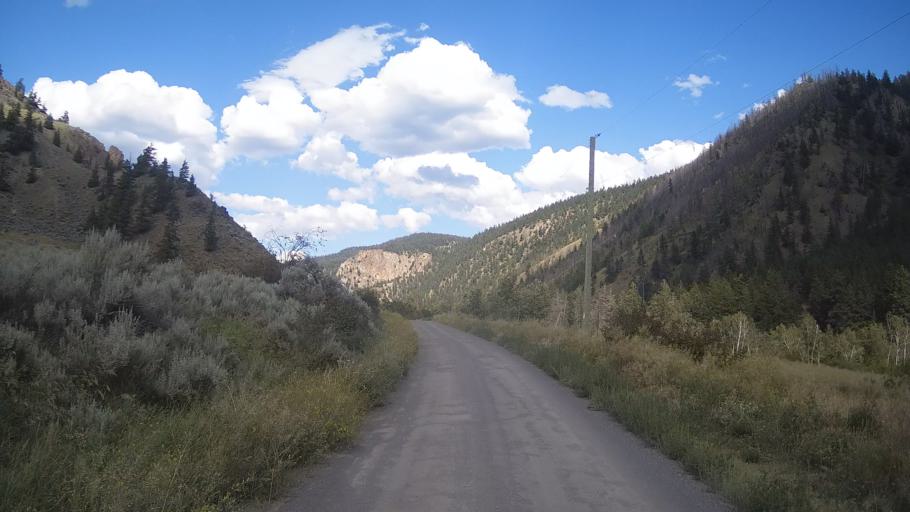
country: CA
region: British Columbia
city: Lillooet
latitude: 51.2201
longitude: -122.0785
